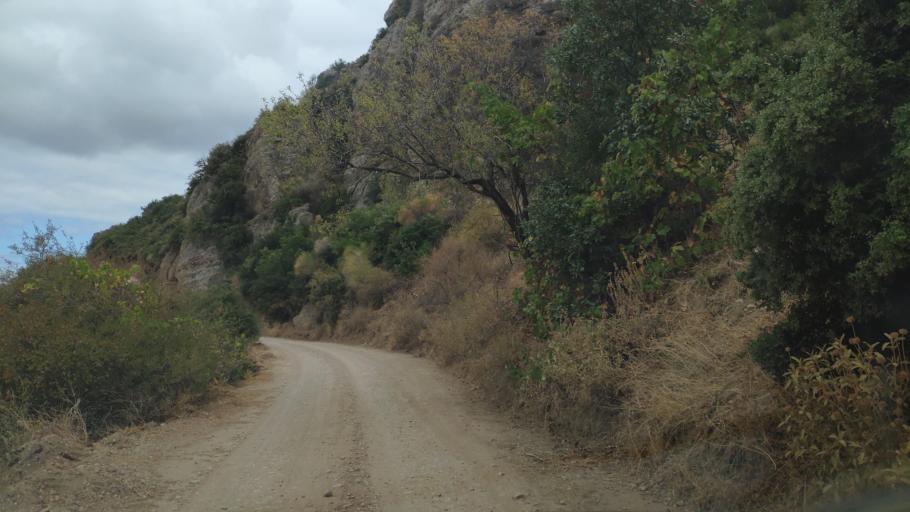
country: GR
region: West Greece
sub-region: Nomos Achaias
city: Temeni
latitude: 38.1592
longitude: 22.1421
